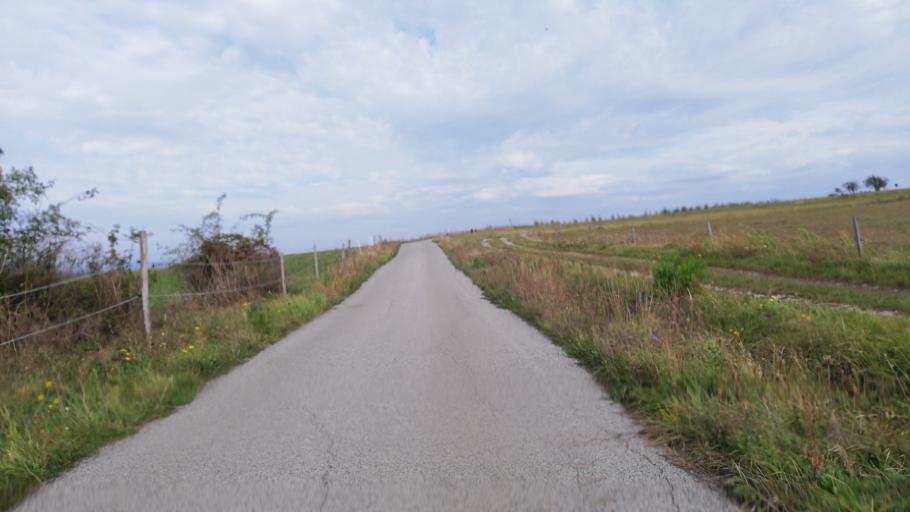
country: CZ
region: South Moravian
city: Sudomerice
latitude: 48.8400
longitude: 17.2859
